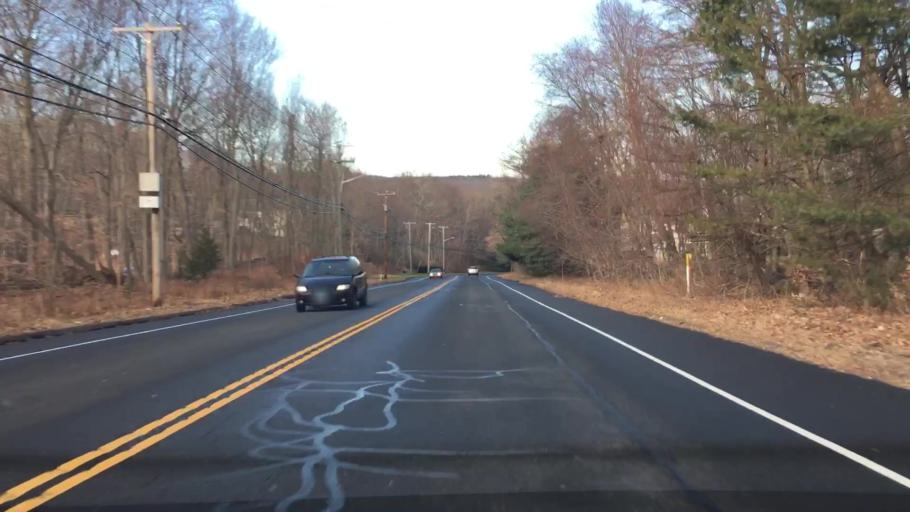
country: US
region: Connecticut
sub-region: Fairfield County
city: Shelton
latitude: 41.3011
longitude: -73.0943
